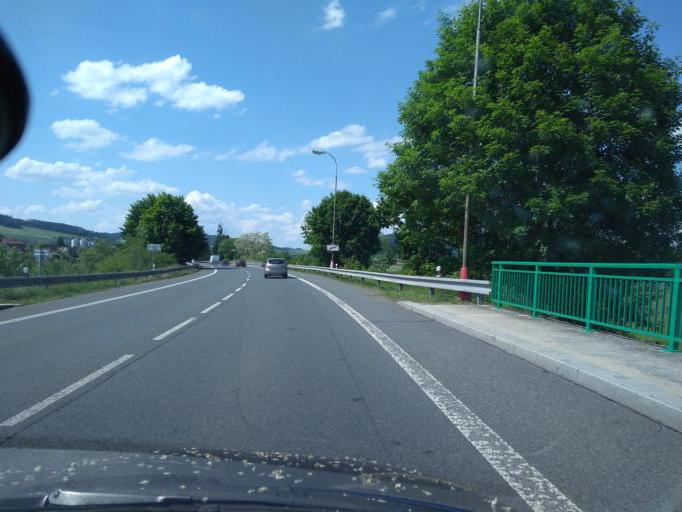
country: CZ
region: Plzensky
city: Svihov
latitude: 49.4825
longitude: 13.2886
